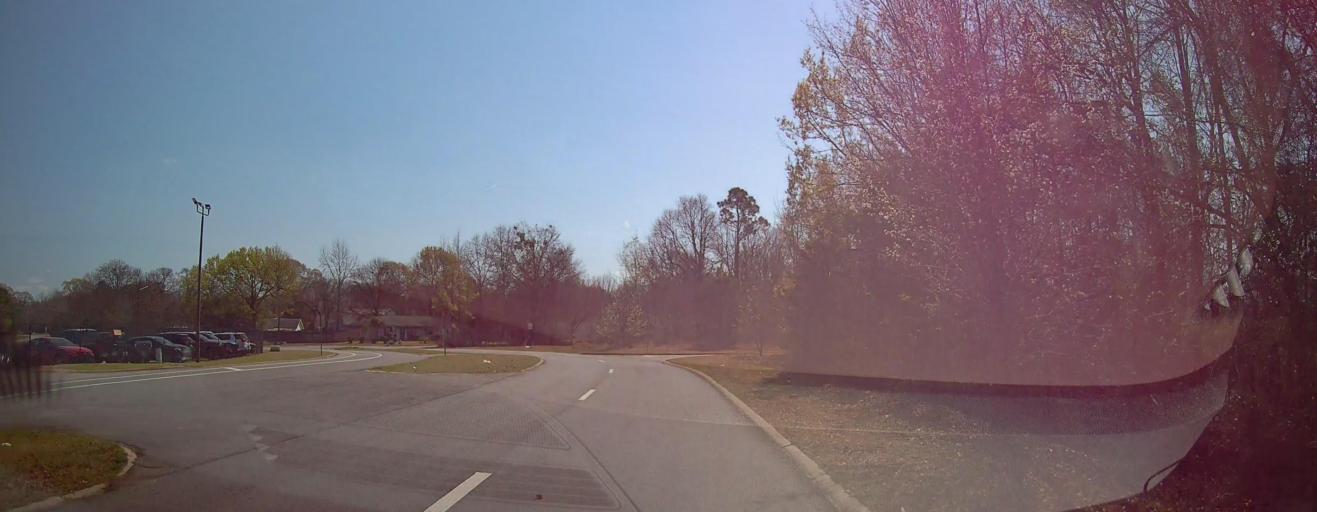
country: US
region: Georgia
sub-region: Houston County
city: Centerville
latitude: 32.6149
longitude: -83.6789
